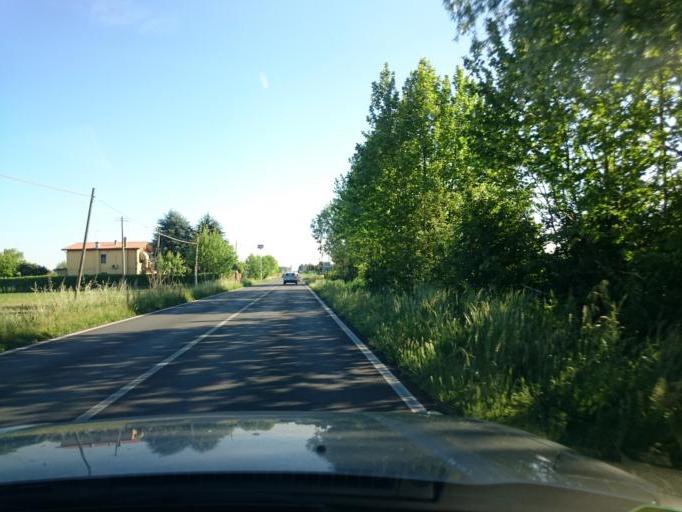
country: IT
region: Veneto
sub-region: Provincia di Venezia
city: Pianiga
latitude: 45.4709
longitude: 11.9985
